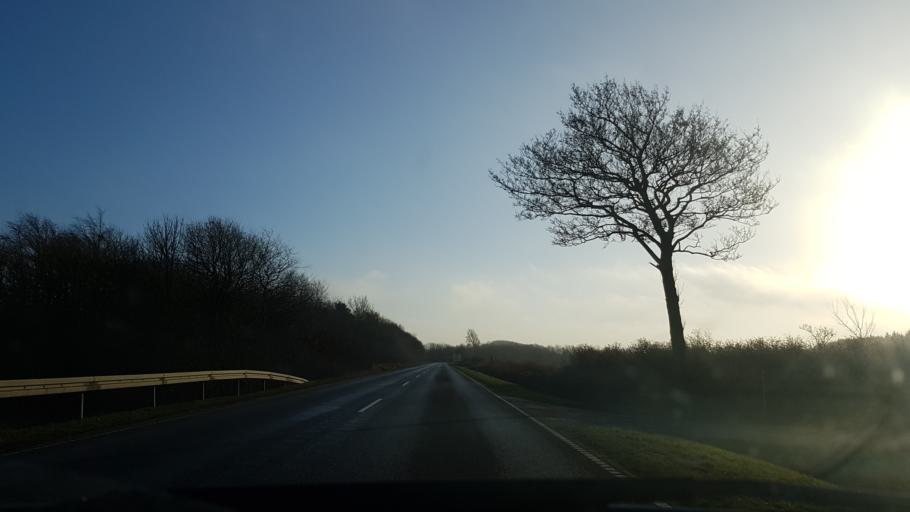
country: DK
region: South Denmark
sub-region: Haderslev Kommune
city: Vojens
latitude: 55.2022
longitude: 9.1942
